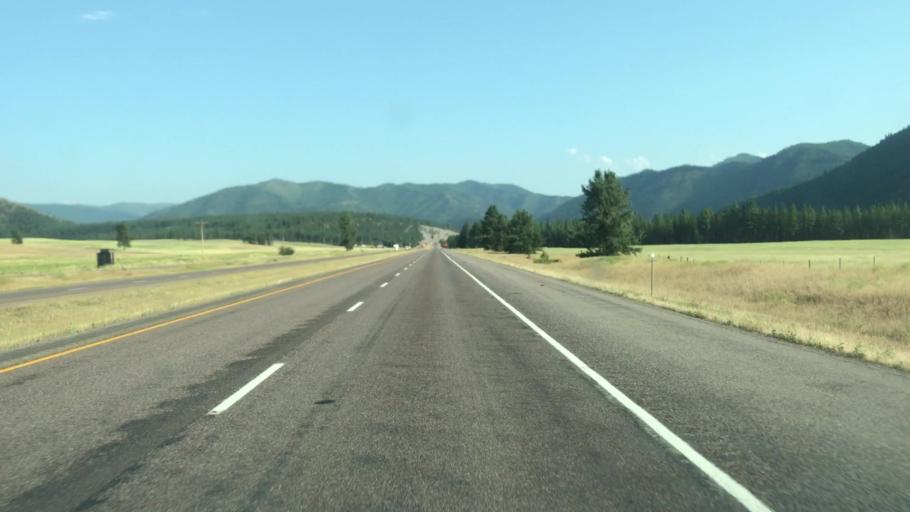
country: US
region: Montana
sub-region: Mineral County
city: Superior
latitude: 47.0421
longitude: -114.7503
